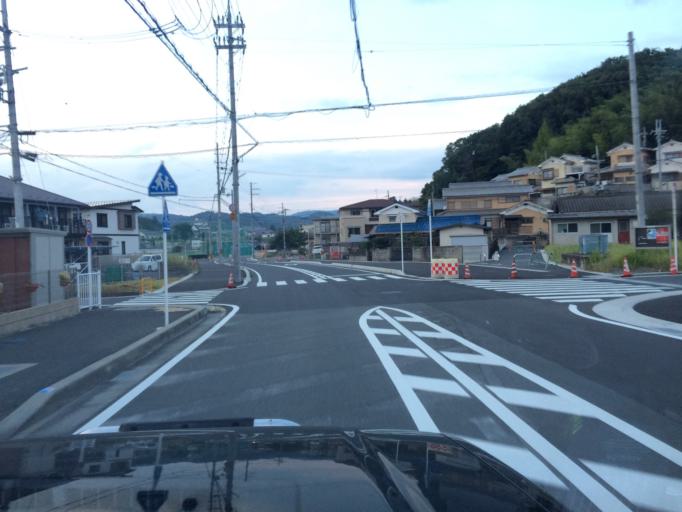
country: JP
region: Kyoto
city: Kameoka
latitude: 35.1009
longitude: 135.4744
